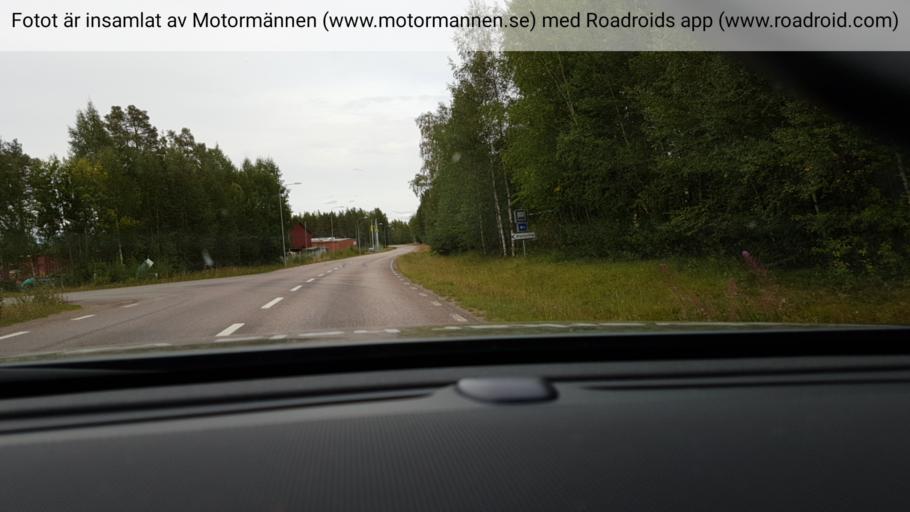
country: NO
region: Hedmark
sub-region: Trysil
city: Innbygda
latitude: 61.6949
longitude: 13.1113
